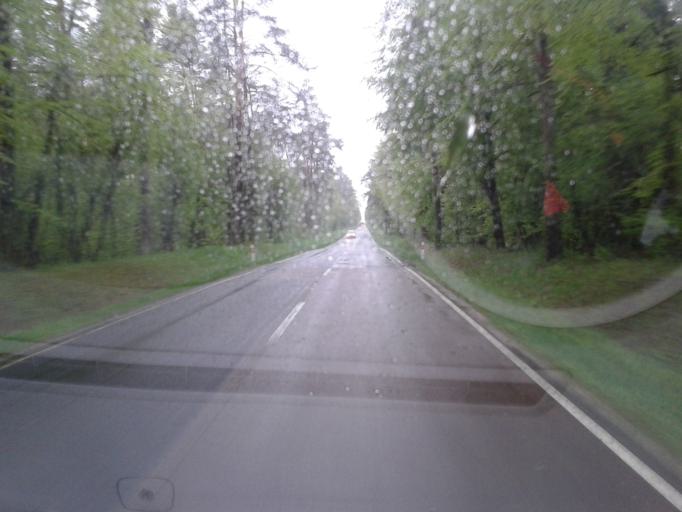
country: PL
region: Subcarpathian Voivodeship
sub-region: Powiat lubaczowski
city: Nowe Siolo
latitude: 50.2968
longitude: 23.2084
